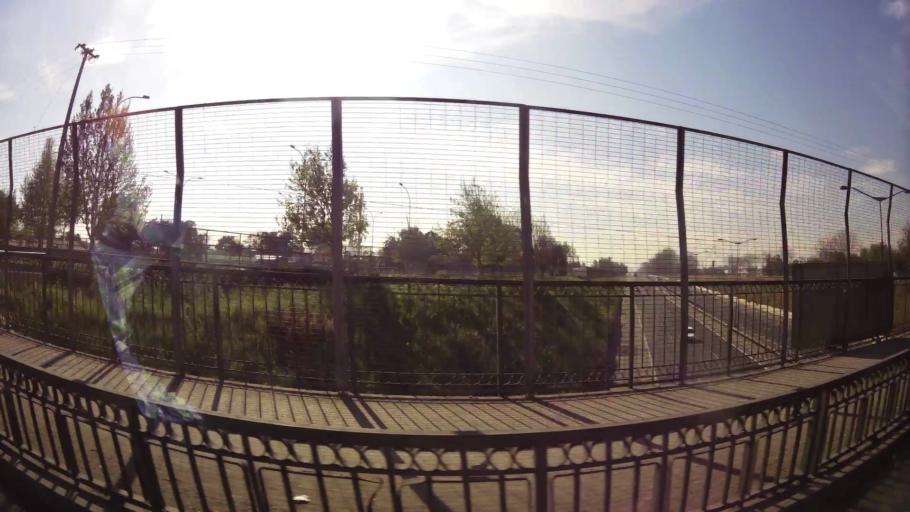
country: CL
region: Santiago Metropolitan
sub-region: Provincia de Santiago
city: Lo Prado
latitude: -33.4534
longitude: -70.7388
